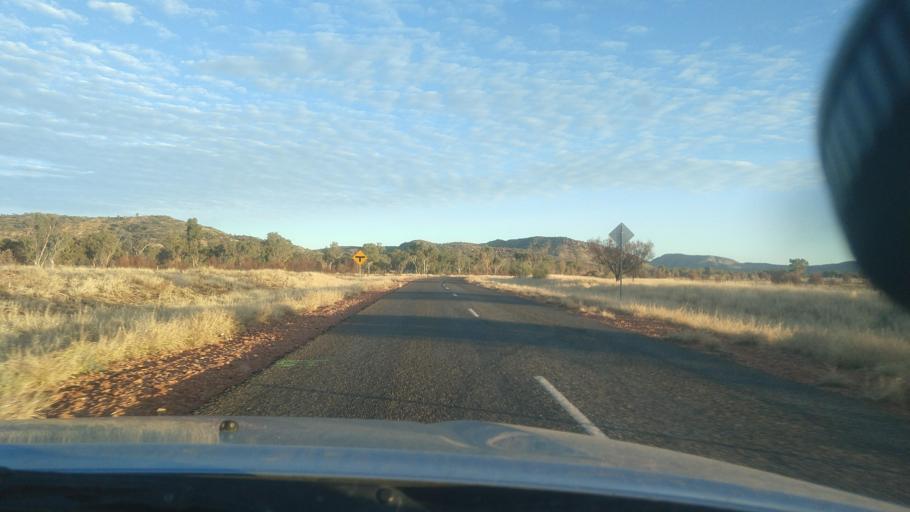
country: AU
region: Northern Territory
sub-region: Alice Springs
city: Alice Springs
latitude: -23.7360
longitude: 133.7406
